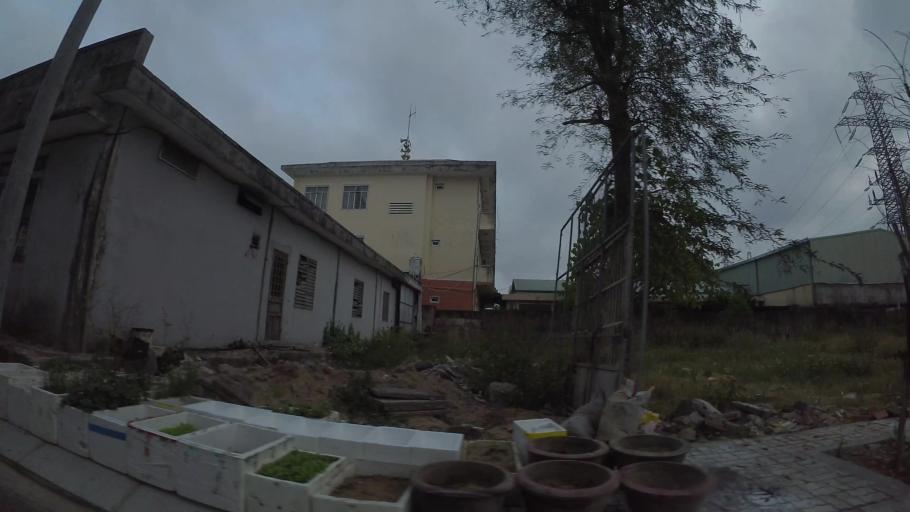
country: VN
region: Da Nang
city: Son Tra
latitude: 16.0392
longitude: 108.2420
